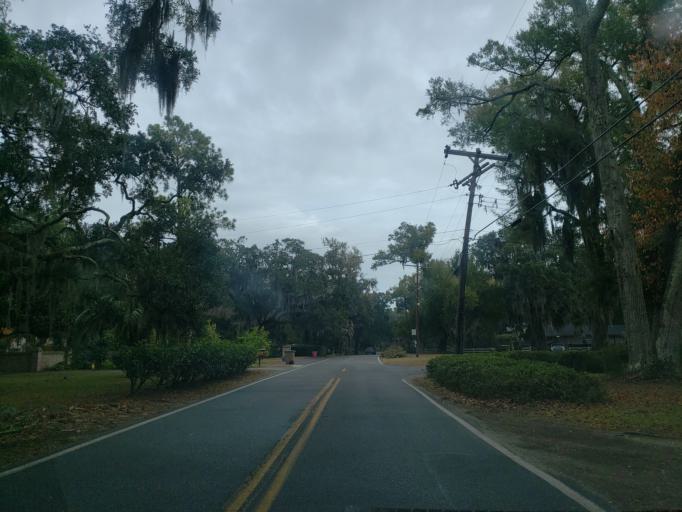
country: US
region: Georgia
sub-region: Chatham County
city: Wilmington Island
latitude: 31.9773
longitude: -80.9995
